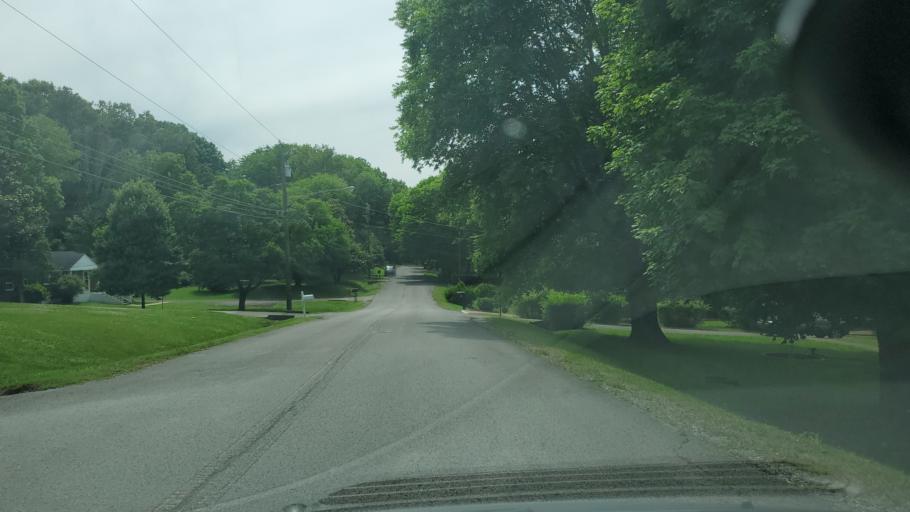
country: US
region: Tennessee
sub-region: Davidson County
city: Oak Hill
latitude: 36.1135
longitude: -86.6966
